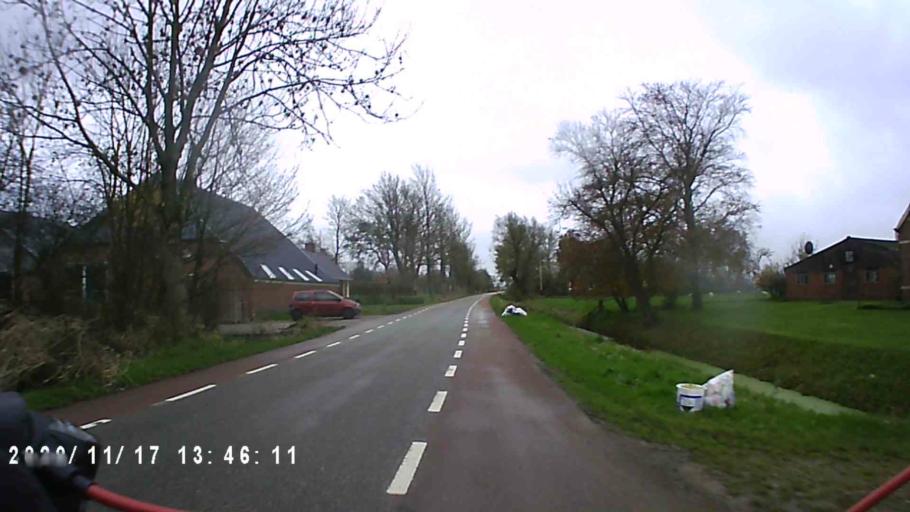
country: NL
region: Groningen
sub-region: Gemeente Zuidhorn
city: Zuidhorn
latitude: 53.2372
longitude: 6.3738
